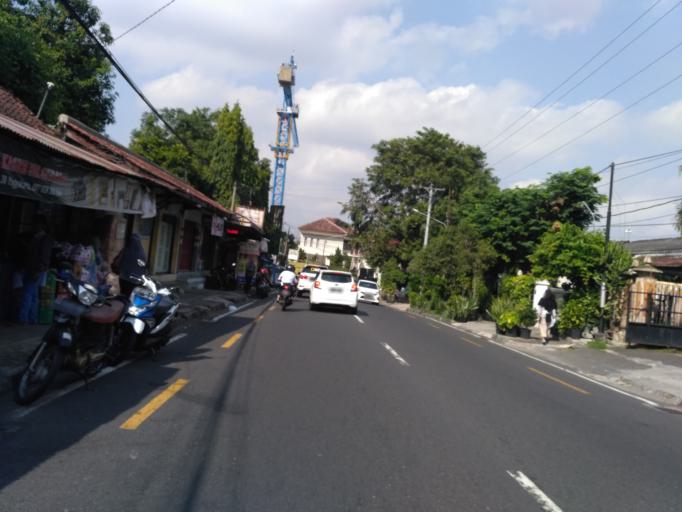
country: ID
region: Daerah Istimewa Yogyakarta
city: Yogyakarta
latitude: -7.7778
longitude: 110.3716
